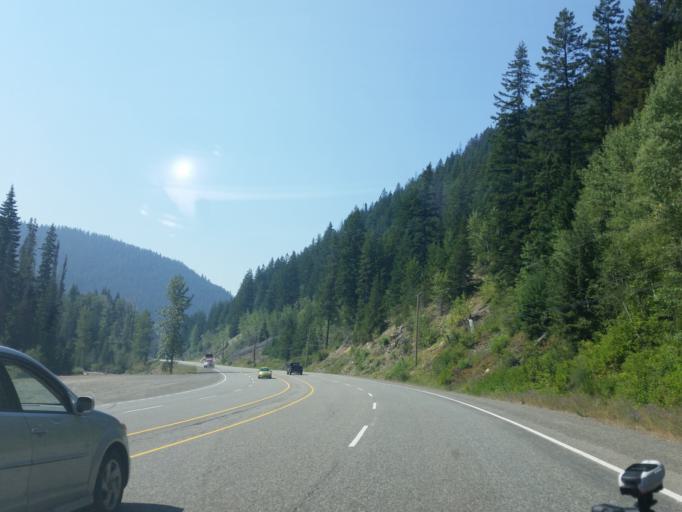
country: CA
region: British Columbia
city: Princeton
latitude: 49.0827
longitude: -120.6939
